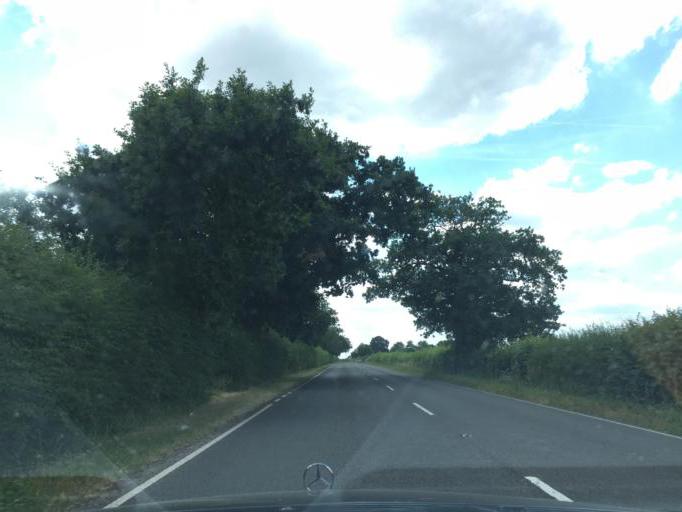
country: GB
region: England
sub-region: Warwickshire
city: Bedworth
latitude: 52.4651
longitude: -1.3951
